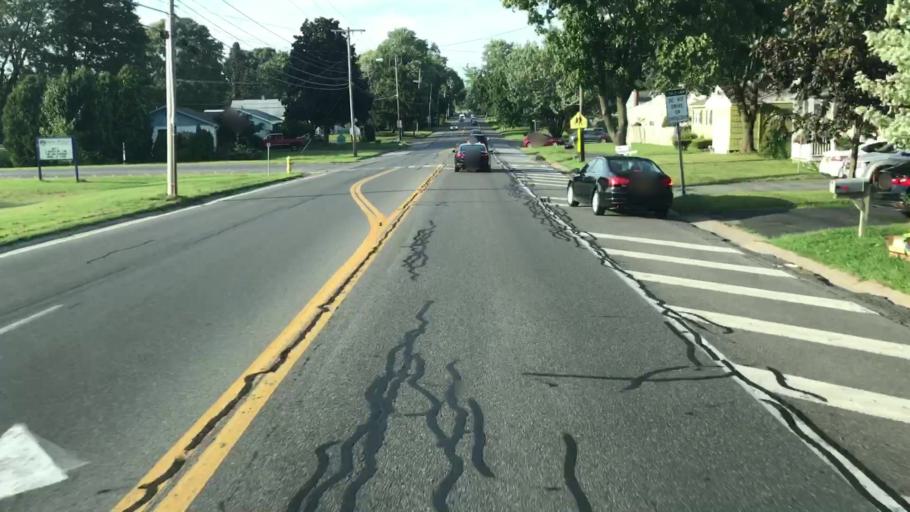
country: US
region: New York
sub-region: Onondaga County
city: Mattydale
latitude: 43.1128
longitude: -76.1598
